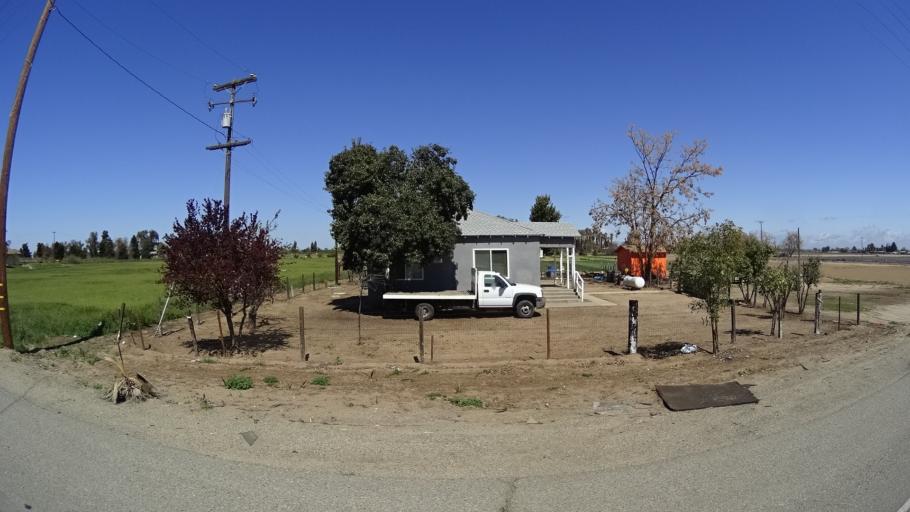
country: US
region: California
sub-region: Fresno County
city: West Park
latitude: 36.7065
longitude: -119.8638
